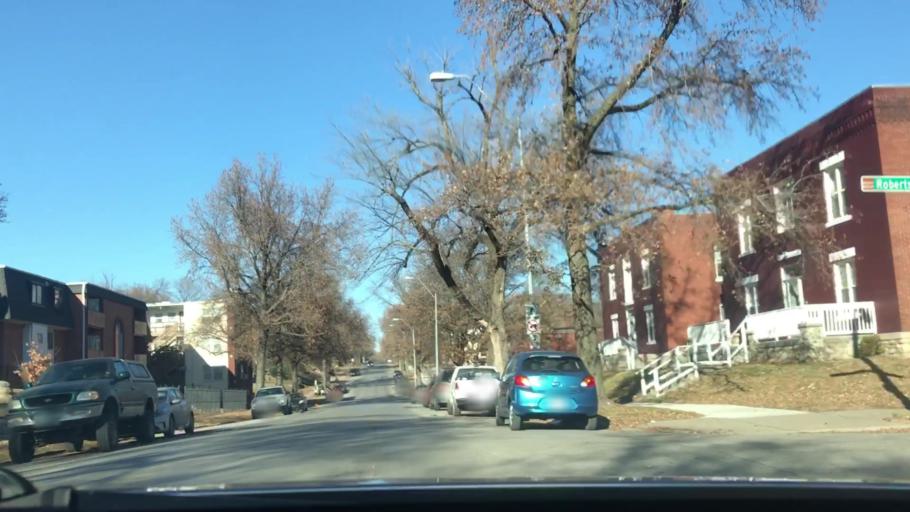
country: US
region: Missouri
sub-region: Clay County
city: North Kansas City
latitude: 39.1070
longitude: -94.5446
